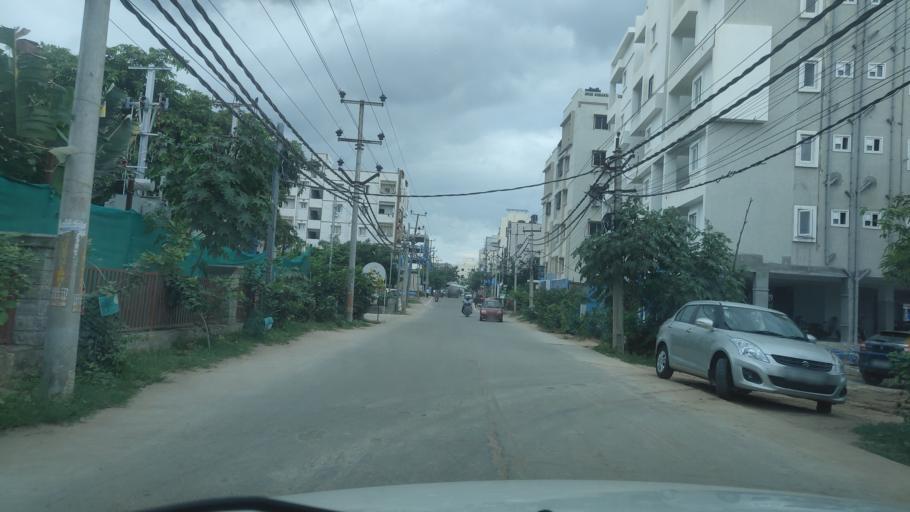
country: IN
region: Telangana
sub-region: Medak
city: Serilingampalle
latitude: 17.4979
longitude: 78.3488
